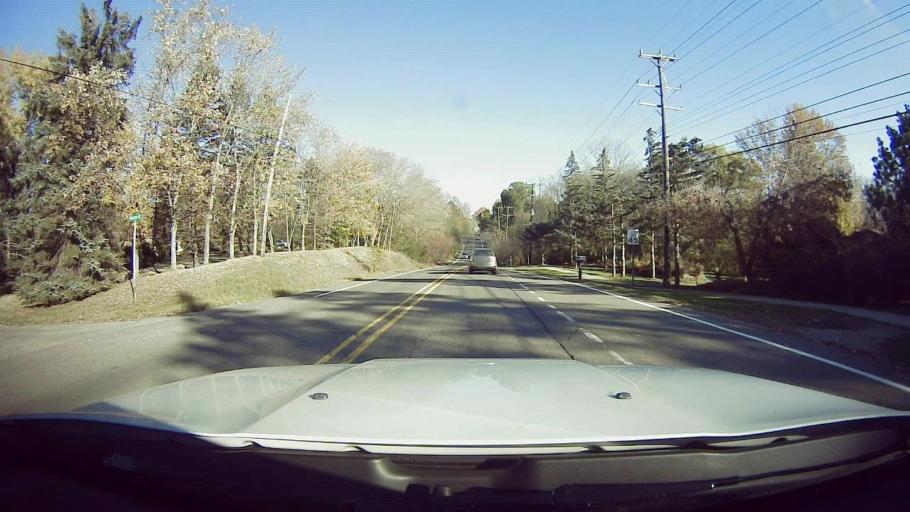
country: US
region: Michigan
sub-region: Oakland County
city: Franklin
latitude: 42.5441
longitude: -83.3108
